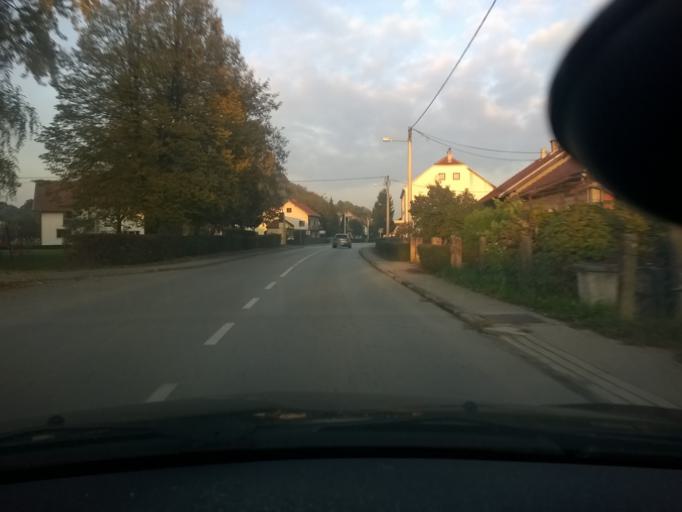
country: HR
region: Krapinsko-Zagorska
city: Zabok
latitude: 46.0182
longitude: 15.8844
